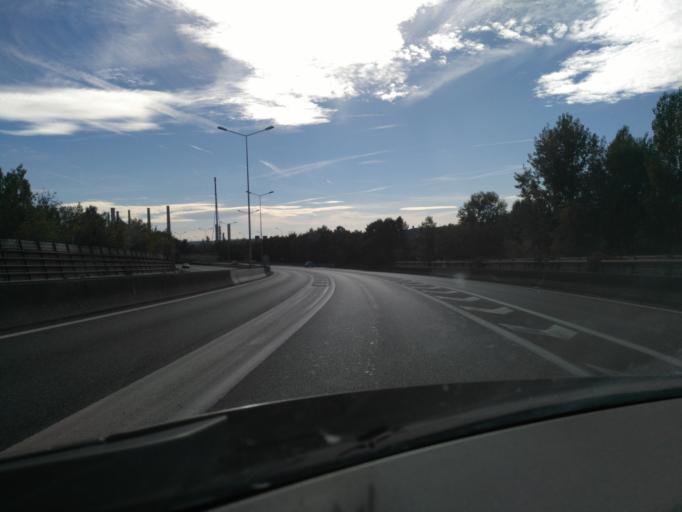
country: FR
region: Rhone-Alpes
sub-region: Departement du Rhone
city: Feyzin
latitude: 45.6830
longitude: 4.8521
